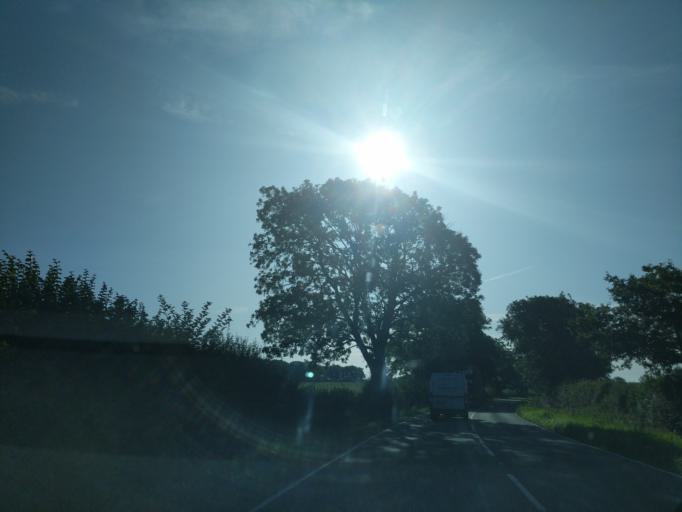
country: GB
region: England
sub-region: District of Rutland
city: Clipsham
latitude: 52.8028
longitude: -0.5793
